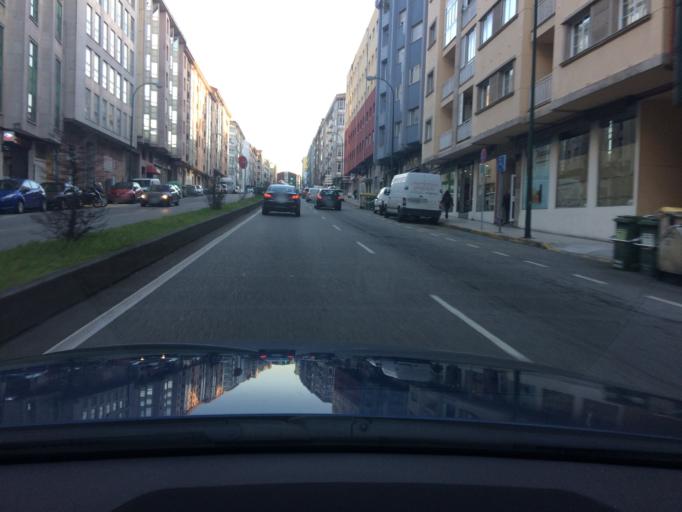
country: ES
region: Galicia
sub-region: Provincia da Coruna
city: Santiago de Compostela
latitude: 42.8471
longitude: -8.5749
